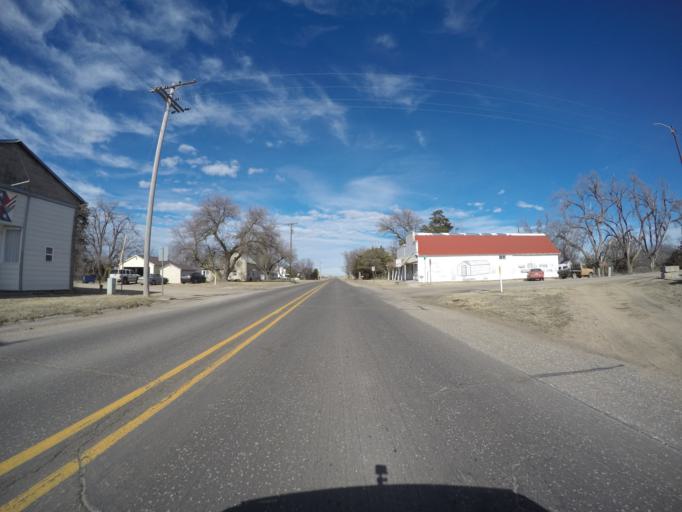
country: US
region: Nebraska
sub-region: Franklin County
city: Franklin
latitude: 40.2048
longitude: -98.9525
